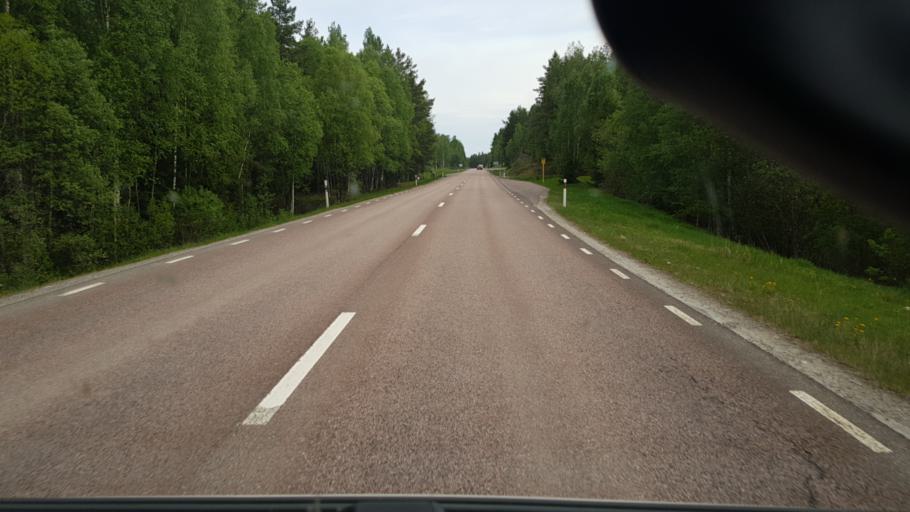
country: SE
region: Vaermland
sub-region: Arvika Kommun
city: Arvika
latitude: 59.6217
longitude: 12.6173
